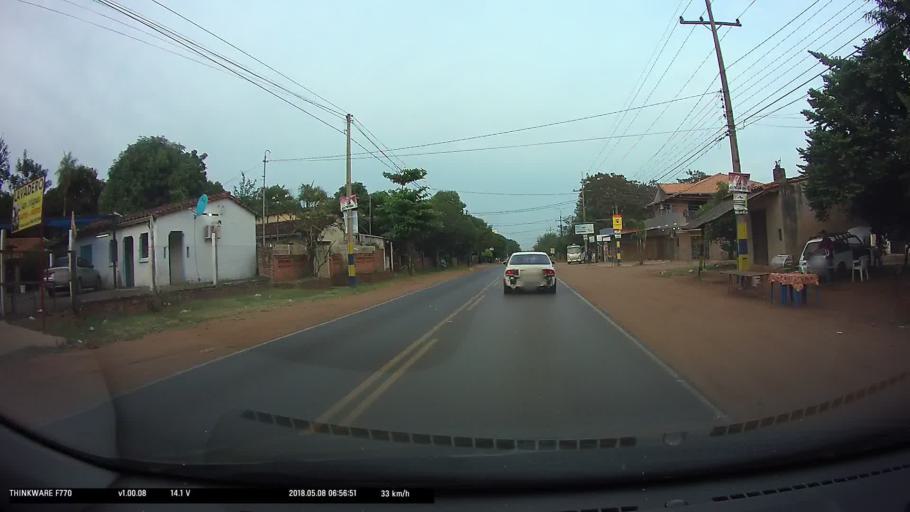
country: PY
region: Central
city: Limpio
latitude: -25.2412
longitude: -57.4754
